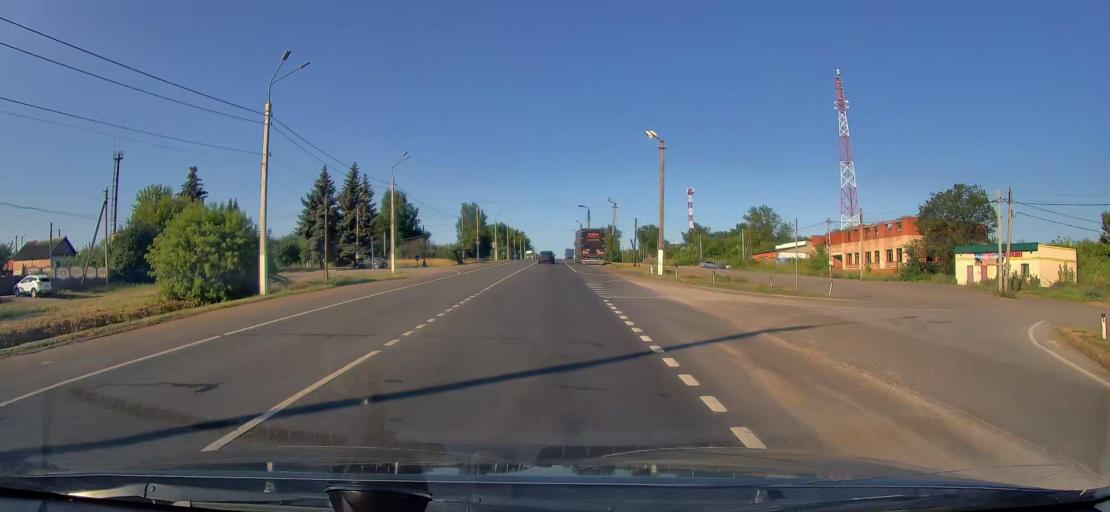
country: RU
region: Tula
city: Plavsk
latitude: 53.6971
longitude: 37.2810
